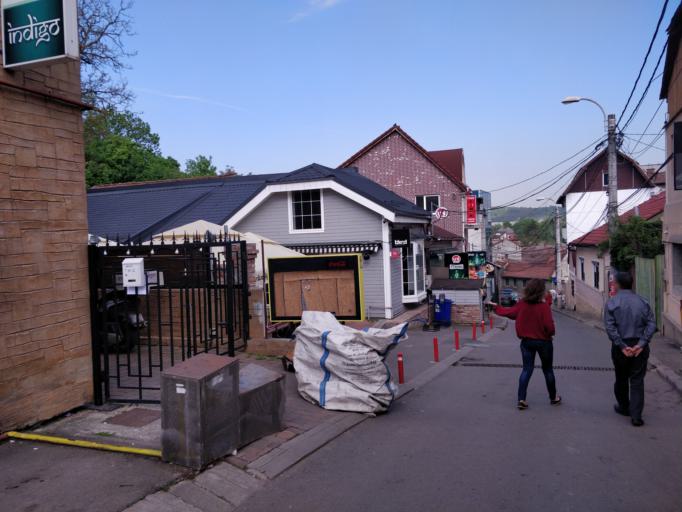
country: RO
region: Cluj
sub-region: Municipiul Cluj-Napoca
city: Cluj-Napoca
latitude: 46.7641
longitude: 23.5766
